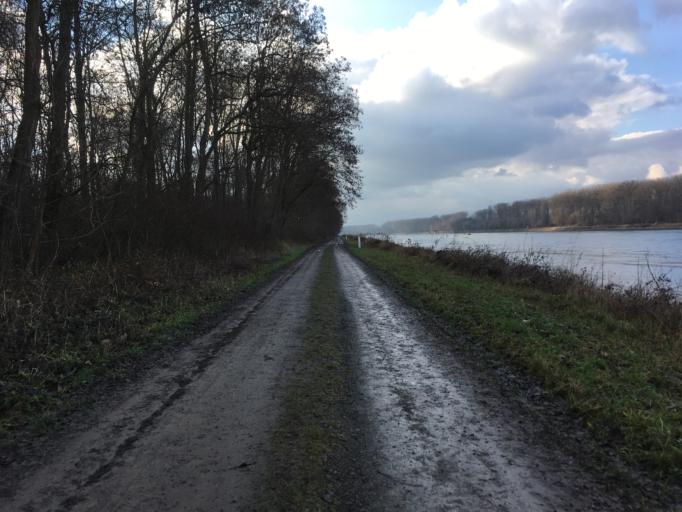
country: DE
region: Baden-Wuerttemberg
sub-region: Karlsruhe Region
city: Philippsburg
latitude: 49.2523
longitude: 8.4223
